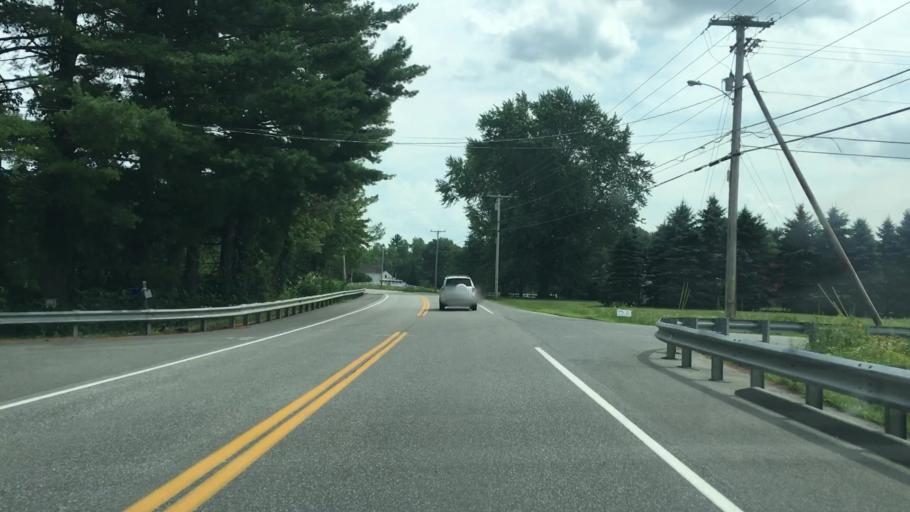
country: US
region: Maine
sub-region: Kennebec County
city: Vassalboro
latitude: 44.4644
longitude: -69.6141
